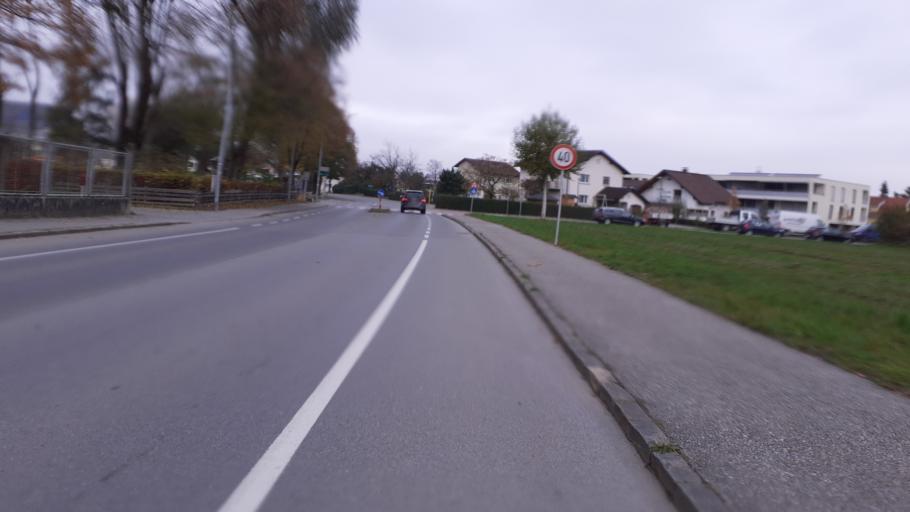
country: AT
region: Vorarlberg
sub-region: Politischer Bezirk Feldkirch
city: Nofels
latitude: 47.2536
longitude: 9.5870
